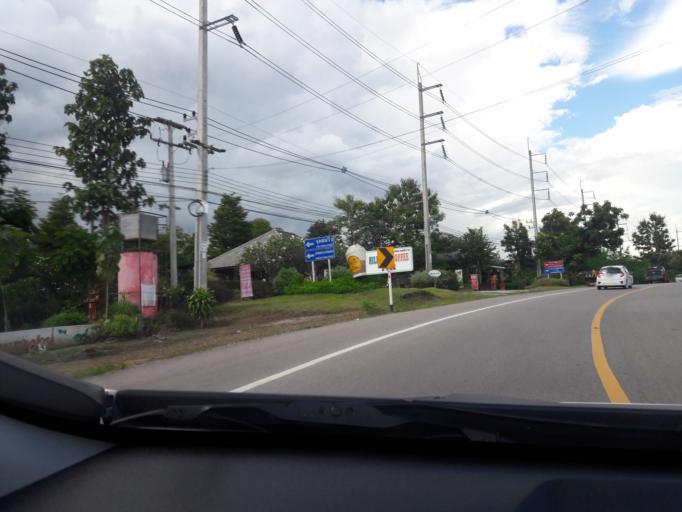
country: TH
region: Mae Hong Son
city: Mae Hi
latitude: 19.3344
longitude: 98.4318
